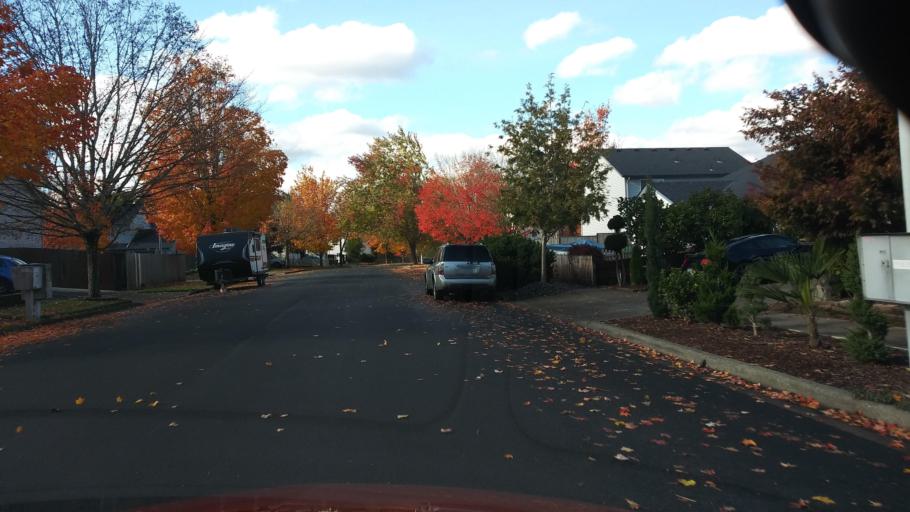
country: US
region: Oregon
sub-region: Washington County
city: Forest Grove
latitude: 45.5331
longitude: -123.1094
